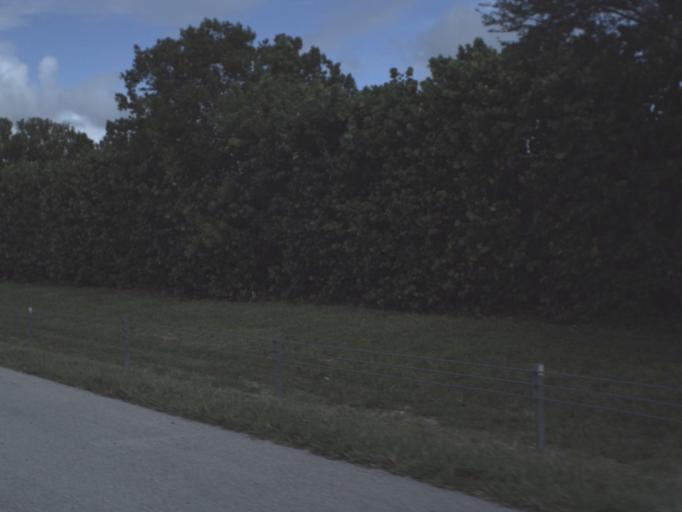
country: US
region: Florida
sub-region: Palm Beach County
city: Boca Del Mar
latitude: 26.3602
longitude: -80.1706
